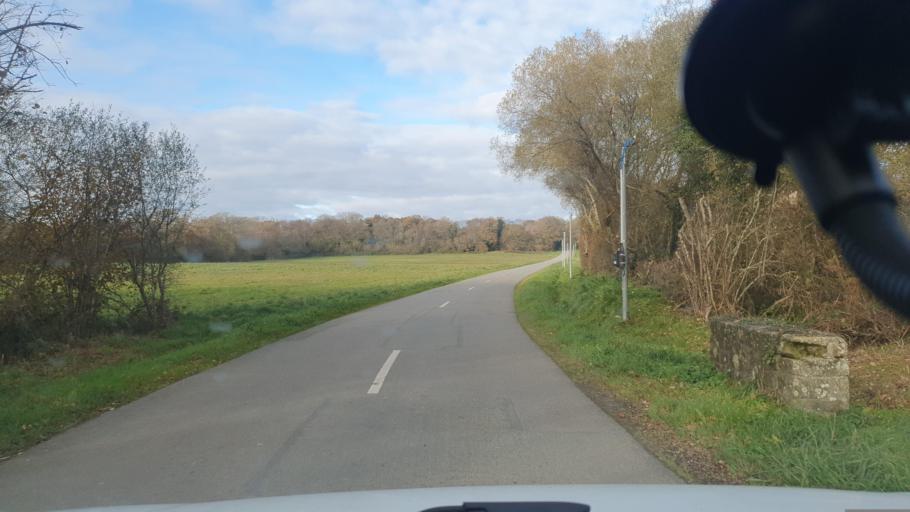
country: FR
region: Brittany
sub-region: Departement du Finistere
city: Briec
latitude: 48.1135
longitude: -3.9948
